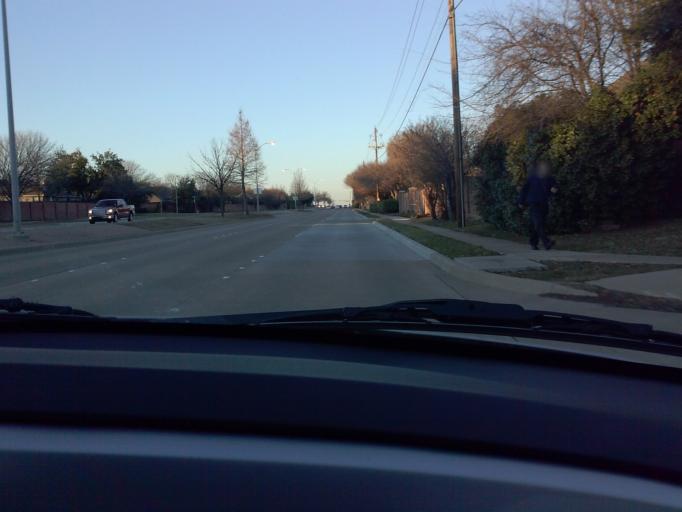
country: US
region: Texas
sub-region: Collin County
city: Plano
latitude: 33.0811
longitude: -96.7499
